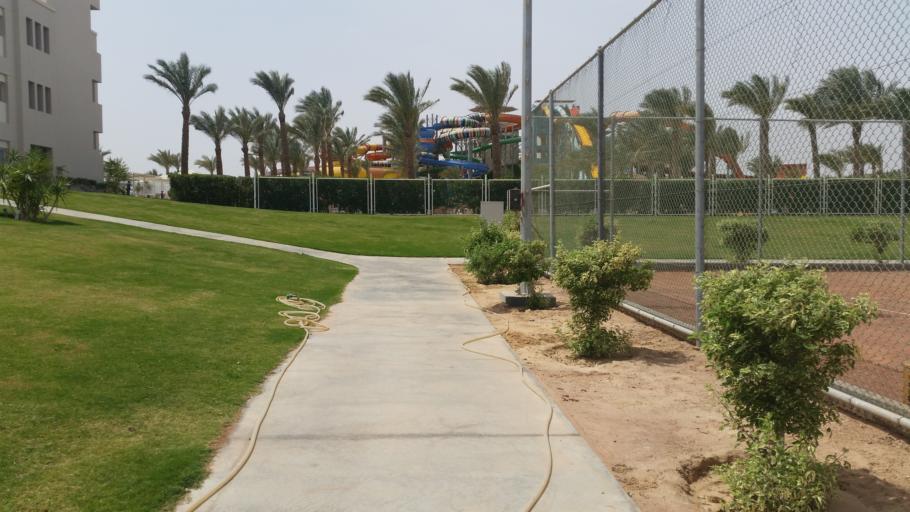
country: EG
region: Red Sea
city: Makadi Bay
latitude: 26.9844
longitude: 33.8742
